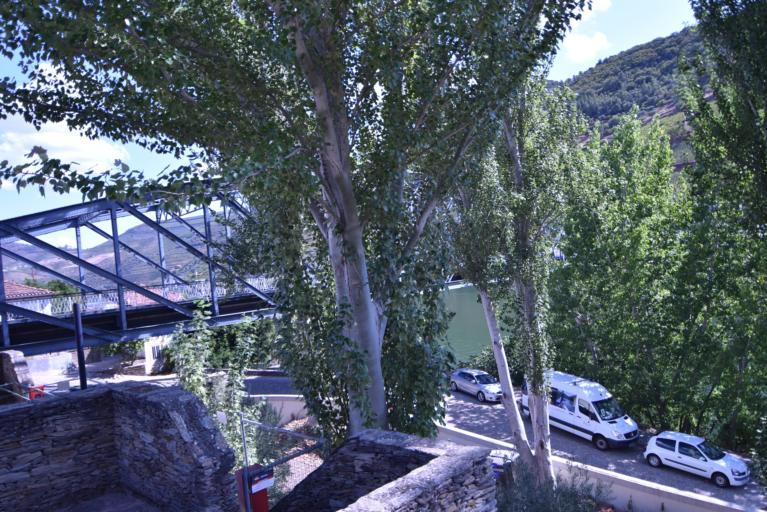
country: PT
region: Vila Real
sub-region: Sabrosa
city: Vilela
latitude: 41.1893
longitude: -7.5425
